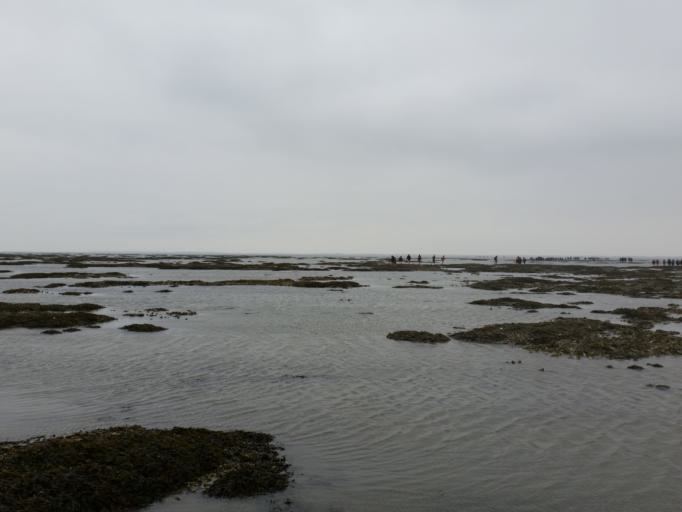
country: NL
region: Friesland
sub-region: Gemeente Dongeradeel
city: Holwerd
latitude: 53.4085
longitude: 5.9241
